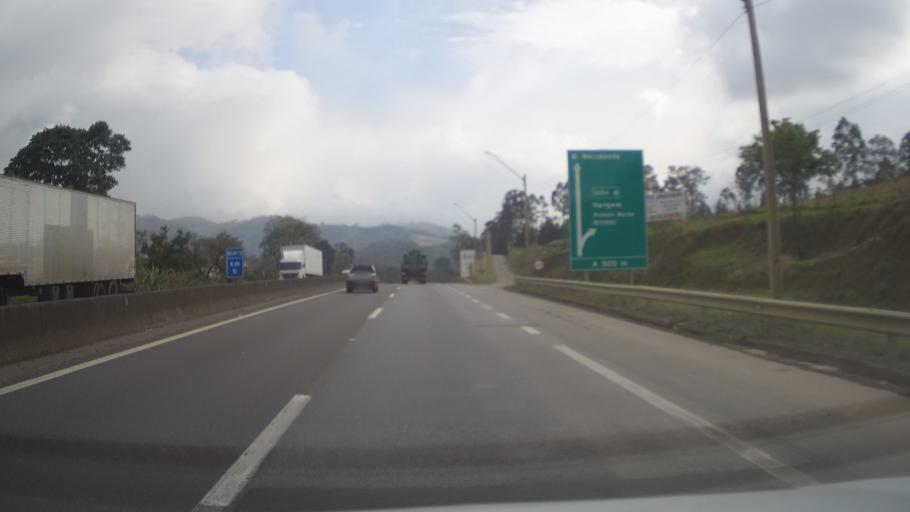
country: BR
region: Minas Gerais
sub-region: Extrema
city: Extrema
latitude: -22.8914
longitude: -46.4136
